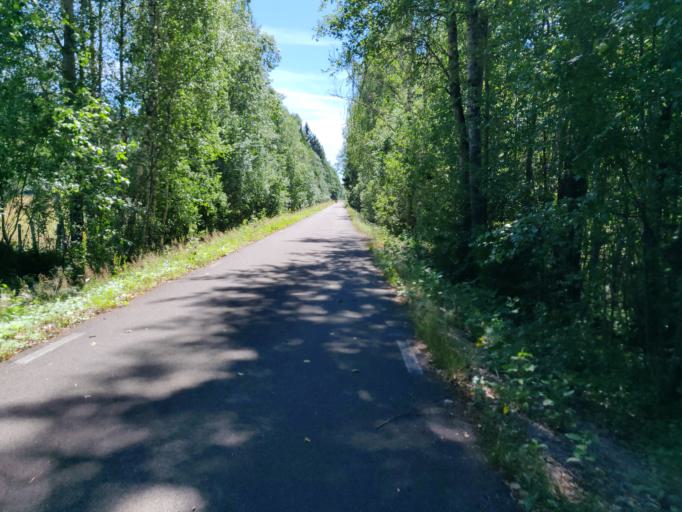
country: SE
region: Vaermland
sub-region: Hagfors Kommun
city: Hagfors
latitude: 59.9820
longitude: 13.5773
